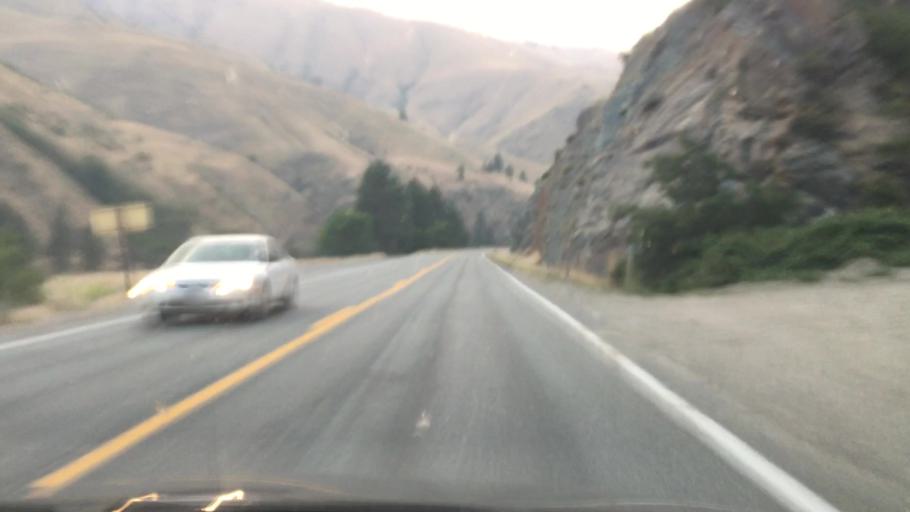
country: US
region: Idaho
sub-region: Idaho County
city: Grangeville
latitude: 45.5654
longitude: -116.3023
